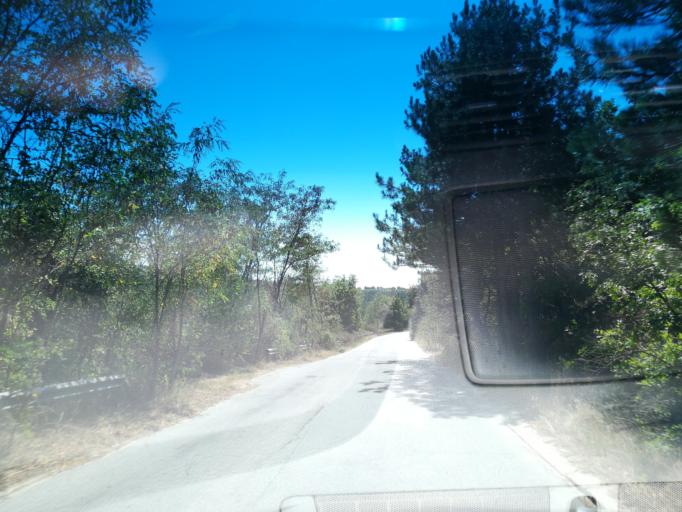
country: BG
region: Pazardzhik
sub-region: Obshtina Strelcha
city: Strelcha
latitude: 42.5314
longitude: 24.3311
